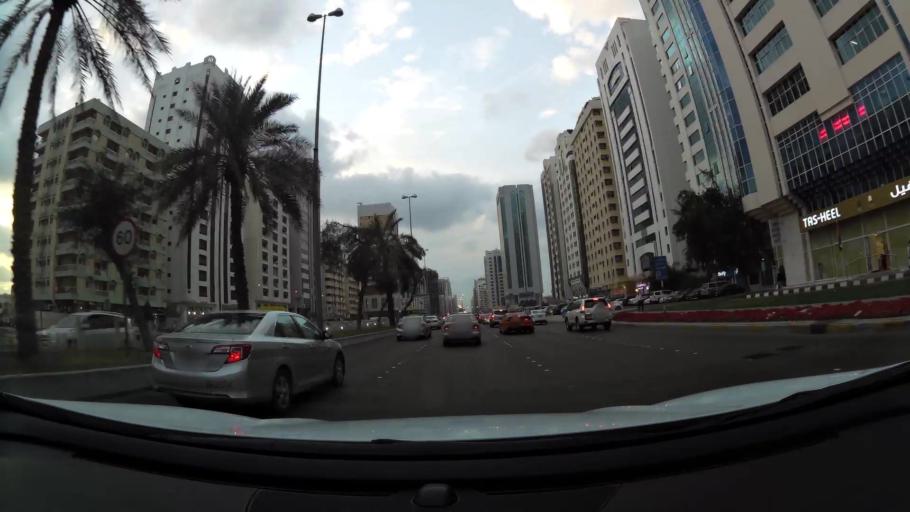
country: AE
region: Abu Dhabi
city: Abu Dhabi
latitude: 24.4609
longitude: 54.3797
